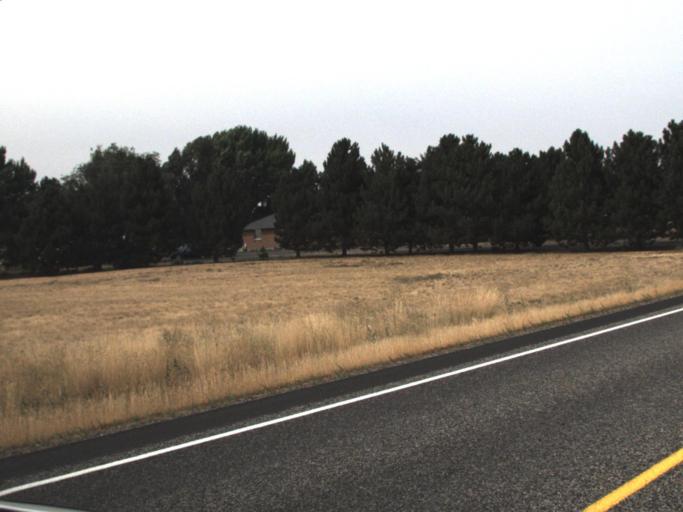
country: US
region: Washington
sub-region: Benton County
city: Benton City
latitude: 46.1214
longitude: -119.6017
